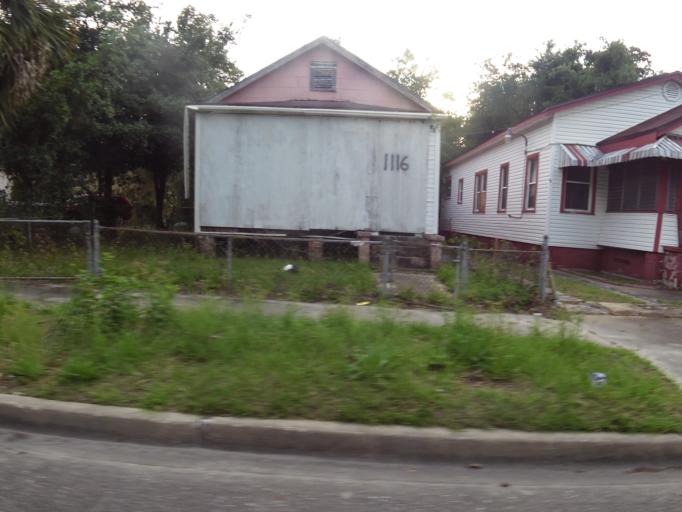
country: US
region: Florida
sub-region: Duval County
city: Jacksonville
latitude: 30.3368
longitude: -81.6441
